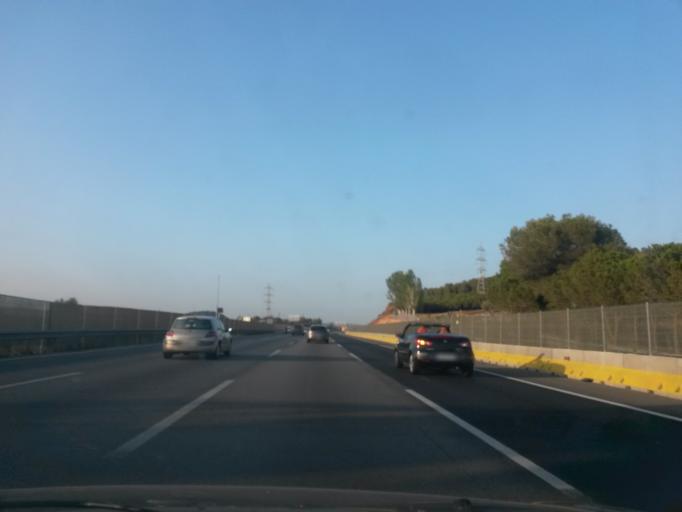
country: ES
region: Catalonia
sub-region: Provincia de Barcelona
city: Castellbisbal
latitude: 41.4563
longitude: 2.0046
